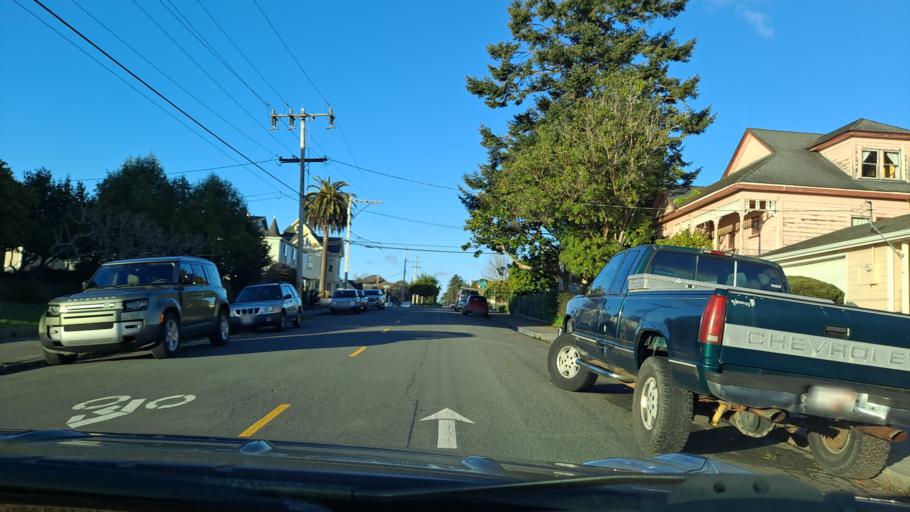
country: US
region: California
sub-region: Humboldt County
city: Arcata
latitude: 40.8726
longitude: -124.0866
